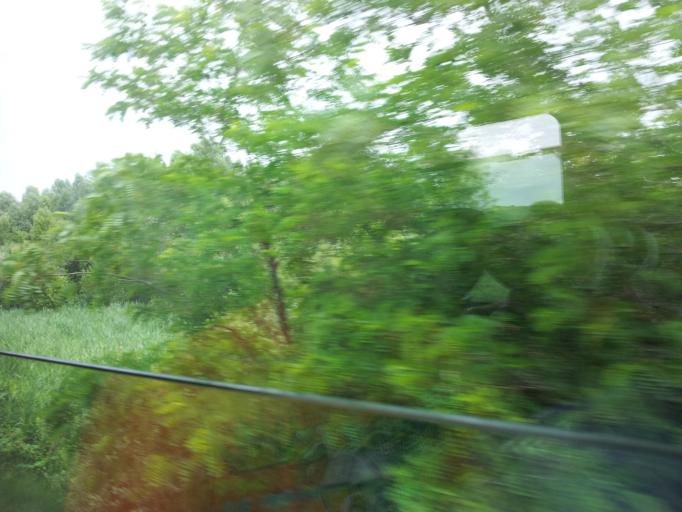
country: HU
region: Veszprem
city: Badacsonytomaj
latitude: 46.8033
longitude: 17.4687
